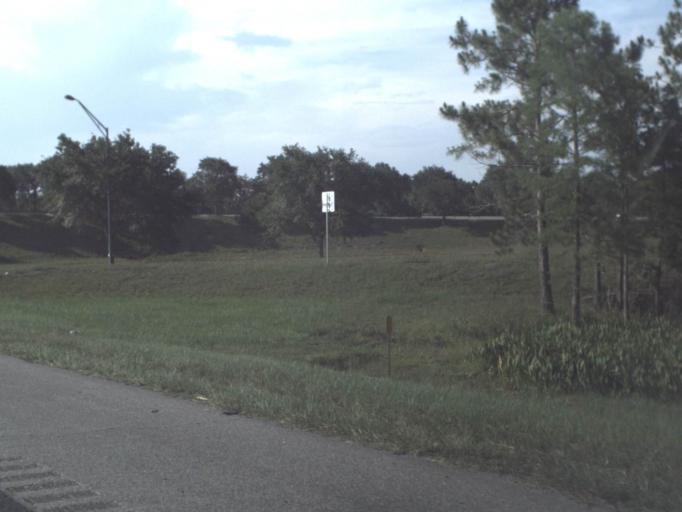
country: US
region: Florida
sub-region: Saint Johns County
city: Villano Beach
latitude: 29.9854
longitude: -81.4612
